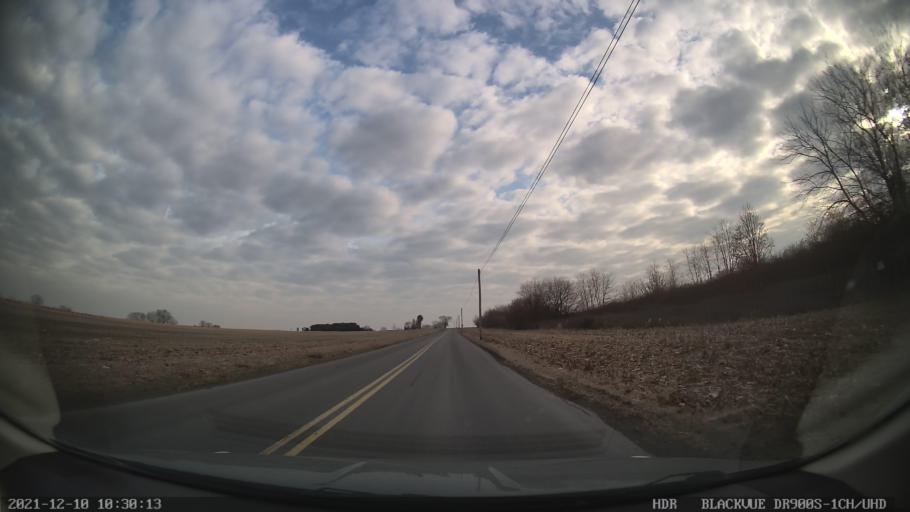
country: US
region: Pennsylvania
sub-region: Berks County
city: Topton
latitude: 40.5168
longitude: -75.7246
